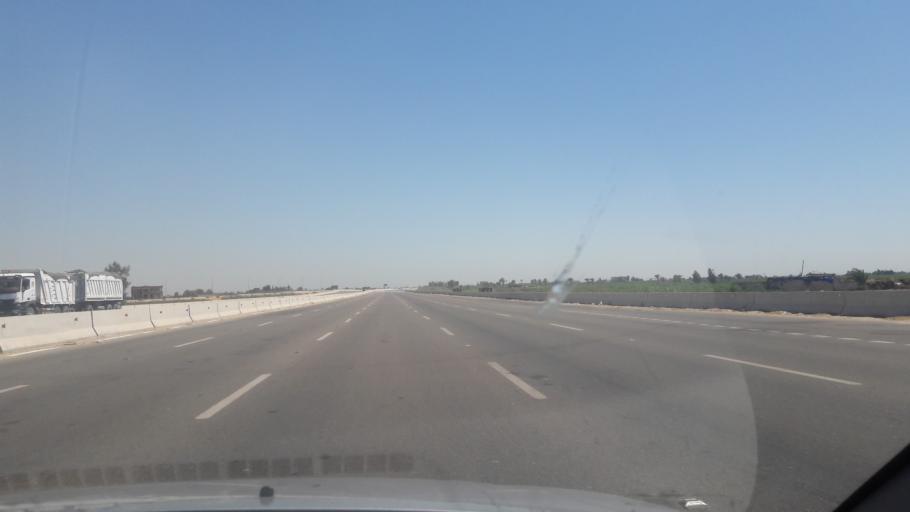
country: EG
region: Muhafazat Bur Sa`id
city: Port Said
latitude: 31.0856
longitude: 32.2335
